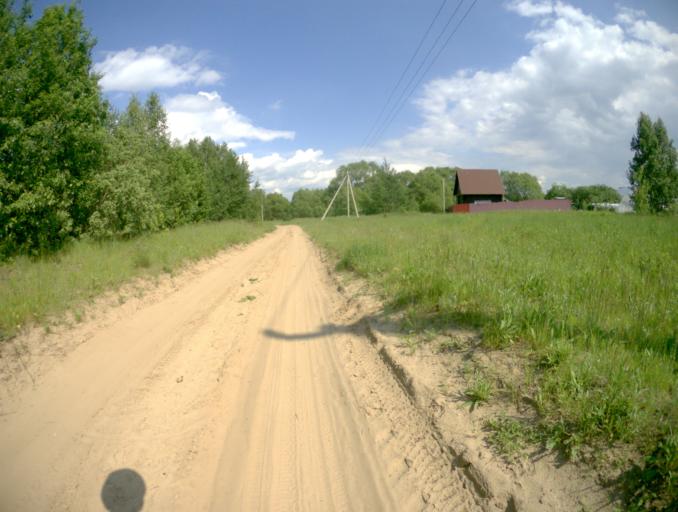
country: RU
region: Vladimir
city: Raduzhnyy
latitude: 56.0282
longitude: 40.3120
